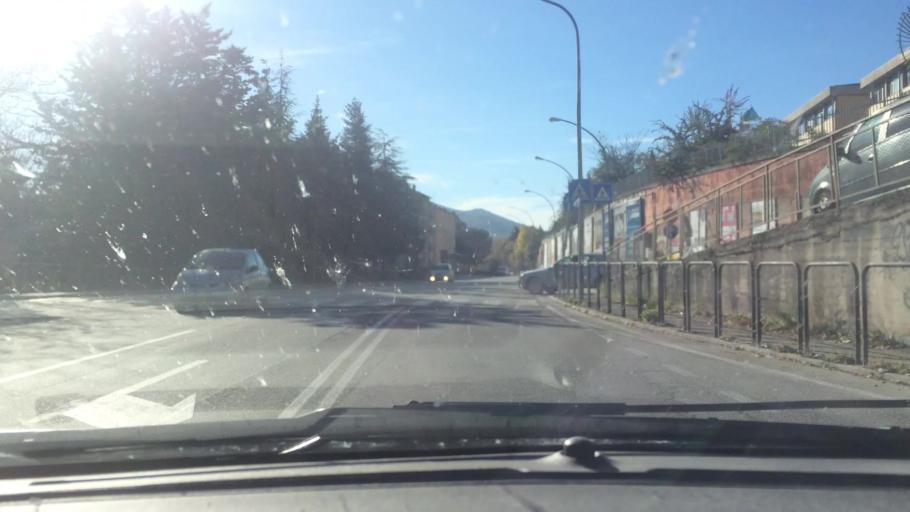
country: IT
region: Basilicate
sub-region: Provincia di Potenza
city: Potenza
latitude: 40.6458
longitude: 15.7953
